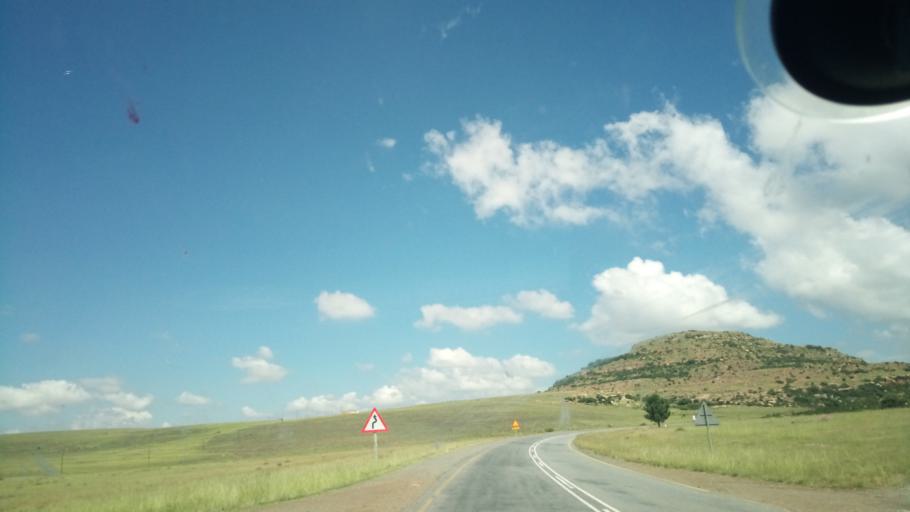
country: ZA
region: Orange Free State
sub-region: Thabo Mofutsanyana District Municipality
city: Ficksburg
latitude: -28.8931
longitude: 27.8495
